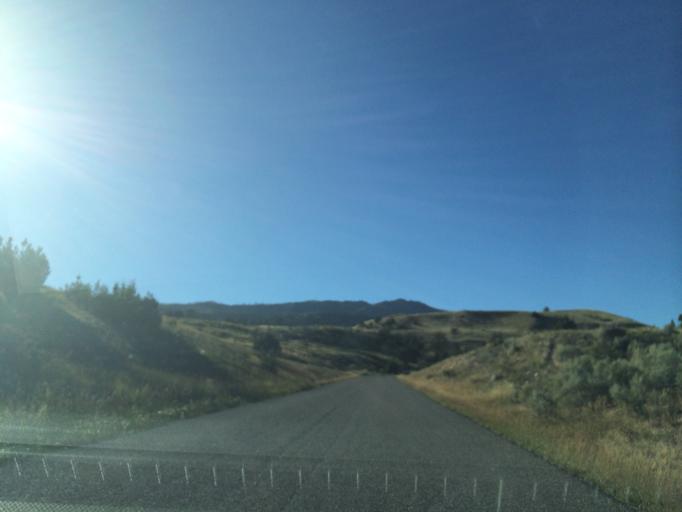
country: US
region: Montana
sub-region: Gallatin County
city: West Yellowstone
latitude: 44.9681
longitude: -110.6951
